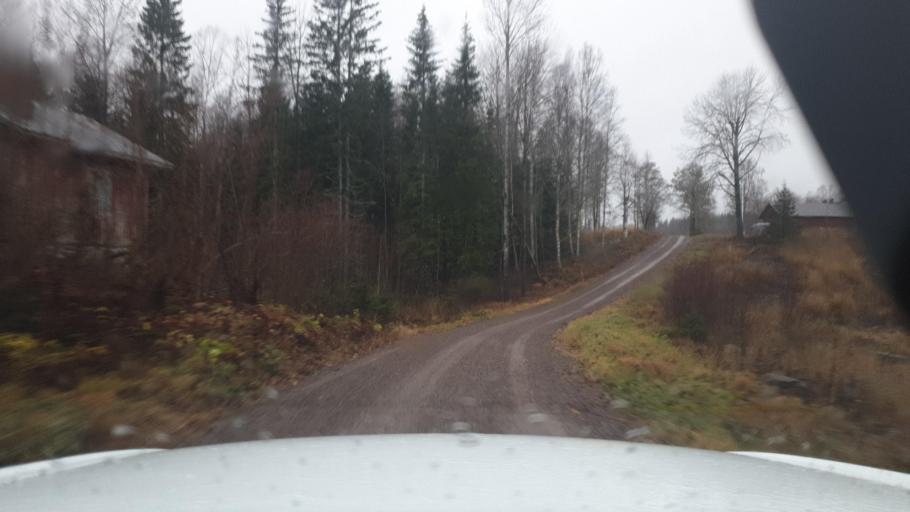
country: SE
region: Vaermland
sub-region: Torsby Kommun
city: Torsby
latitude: 59.9549
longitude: 12.7315
